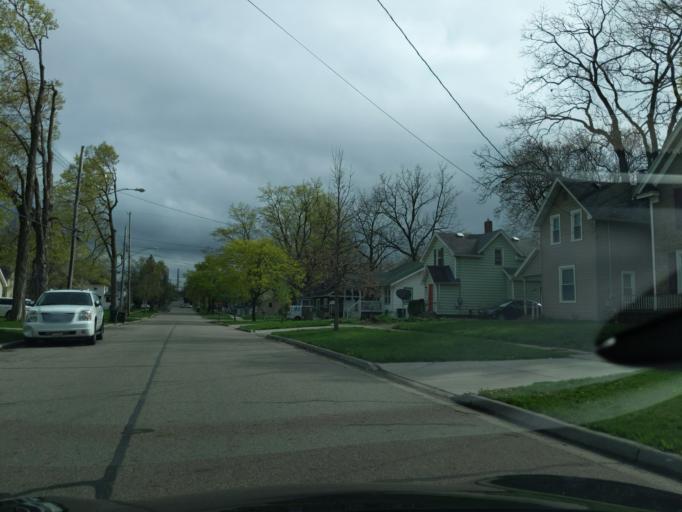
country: US
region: Michigan
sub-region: Ingham County
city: Lansing
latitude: 42.7456
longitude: -84.5584
